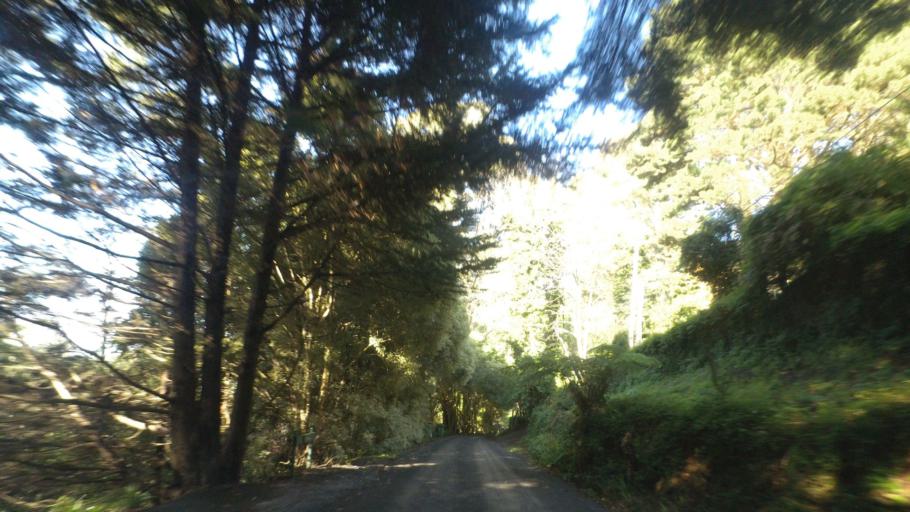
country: AU
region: Victoria
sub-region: Yarra Ranges
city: Mount Dandenong
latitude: -37.8276
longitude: 145.3689
